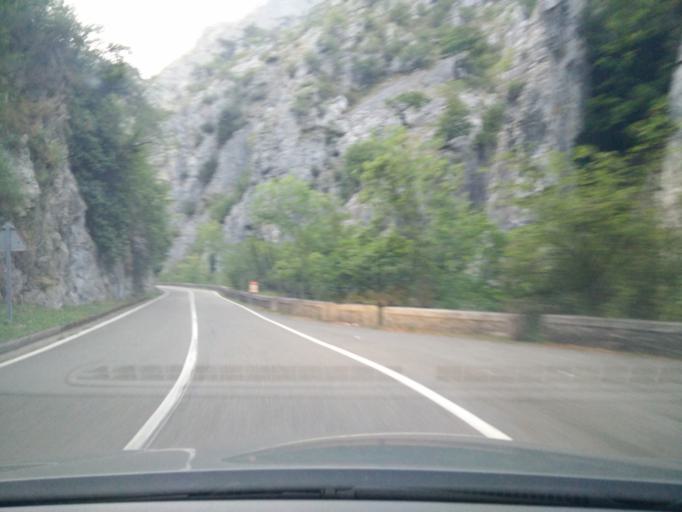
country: ES
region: Castille and Leon
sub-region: Provincia de Leon
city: Oseja de Sajambre
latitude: 43.1531
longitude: -5.0712
